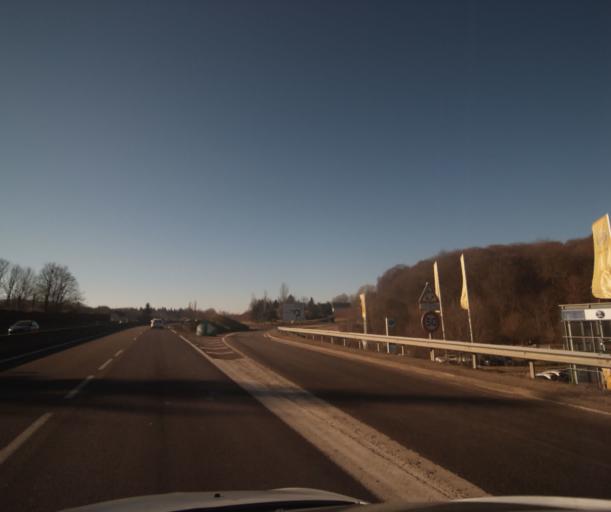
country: FR
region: Franche-Comte
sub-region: Departement du Doubs
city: Franois
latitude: 47.2208
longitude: 5.9408
